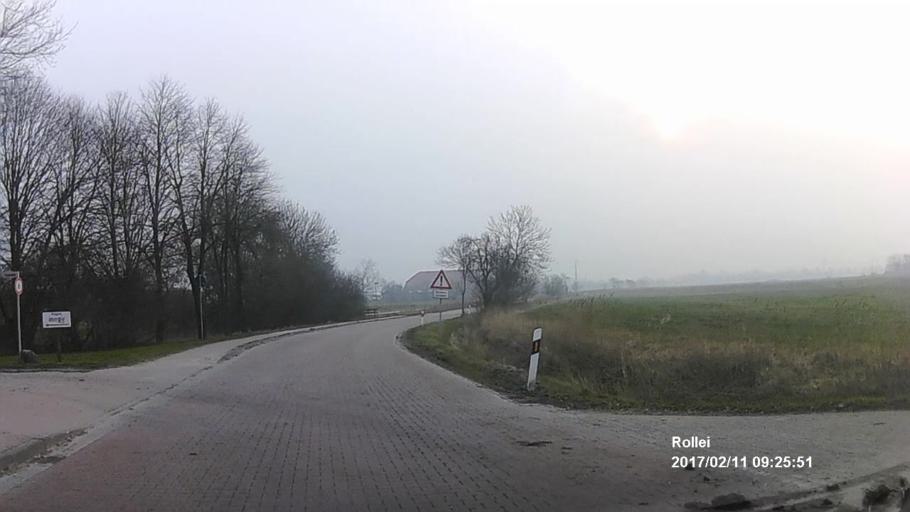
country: DE
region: Lower Saxony
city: Hinte
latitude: 53.4630
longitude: 7.1348
